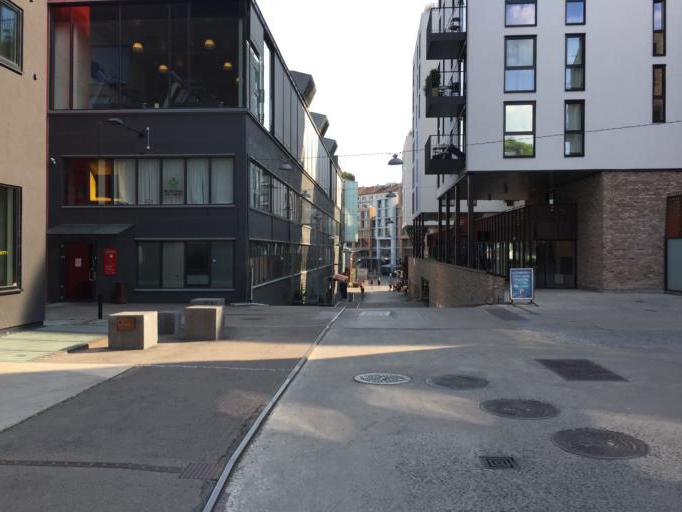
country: NO
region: Oslo
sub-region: Oslo
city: Oslo
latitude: 59.9234
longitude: 10.7521
